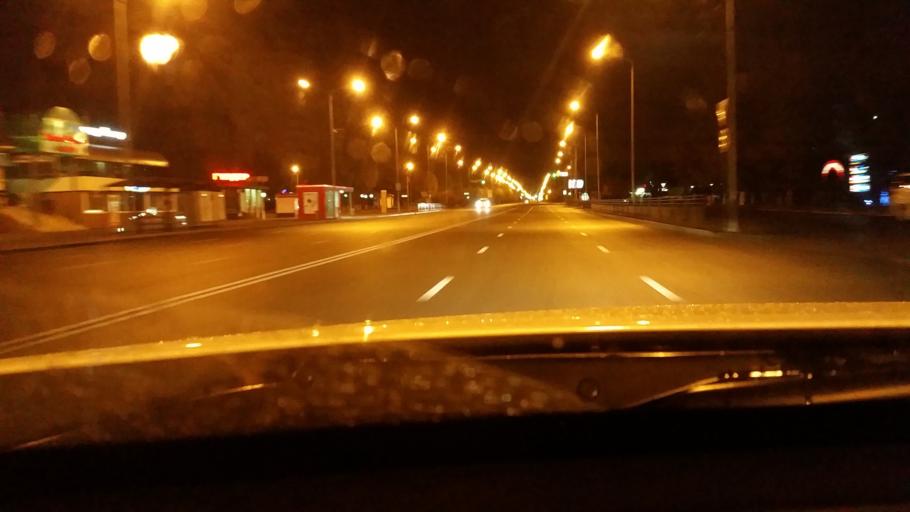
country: KZ
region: Astana Qalasy
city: Astana
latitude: 51.1553
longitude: 71.4840
